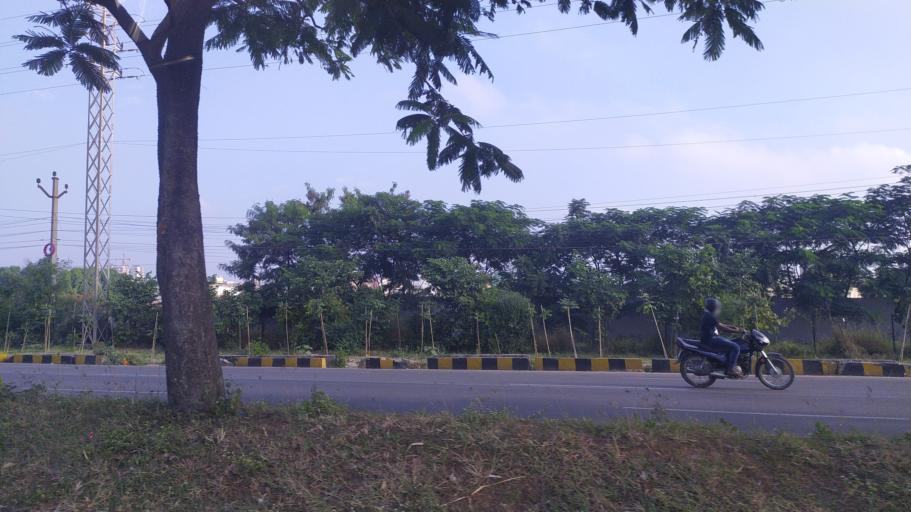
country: IN
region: Telangana
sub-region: Rangareddi
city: Balapur
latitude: 17.3169
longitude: 78.4396
